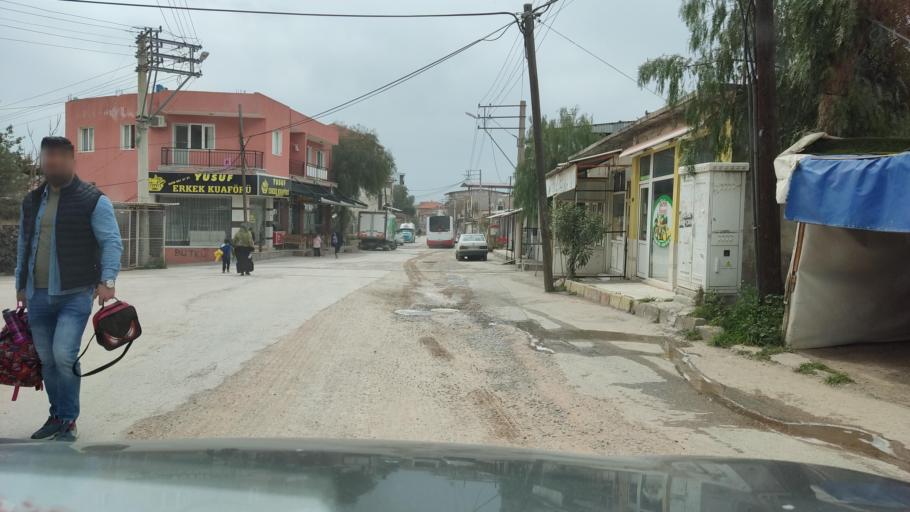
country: TR
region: Izmir
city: Karsiyaka
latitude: 38.4959
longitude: 27.0704
